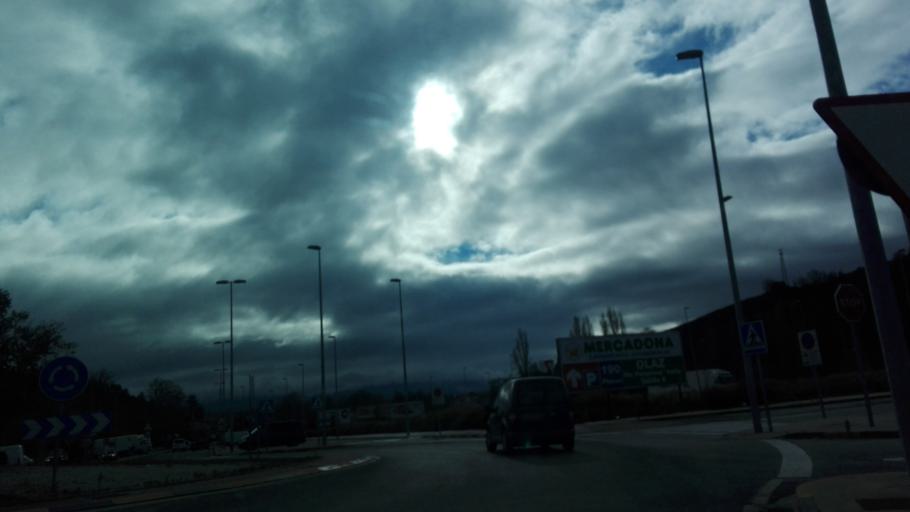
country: ES
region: Navarre
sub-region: Provincia de Navarra
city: Egues-Uharte
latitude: 42.8360
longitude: -1.5864
